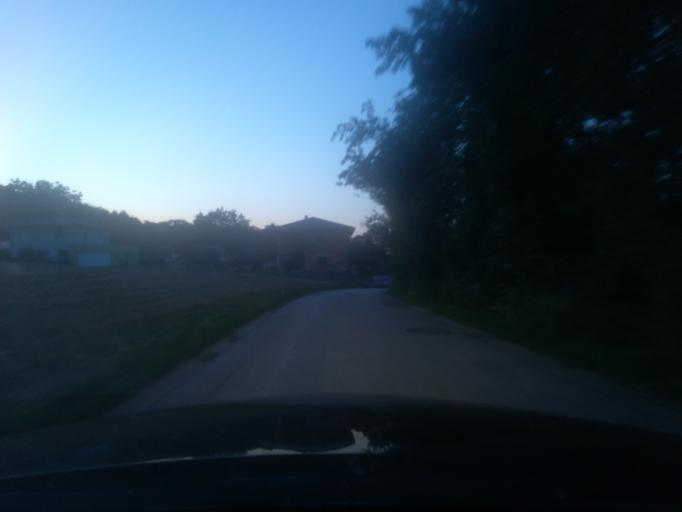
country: AT
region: Upper Austria
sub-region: Wels-Land
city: Thalheim bei Wels
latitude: 48.1568
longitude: 14.0756
